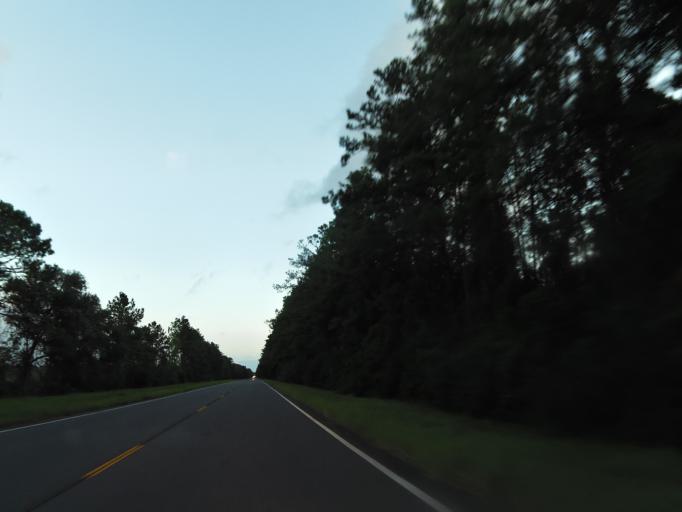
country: US
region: Georgia
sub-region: Camden County
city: Kingsland
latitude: 30.7628
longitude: -81.6873
